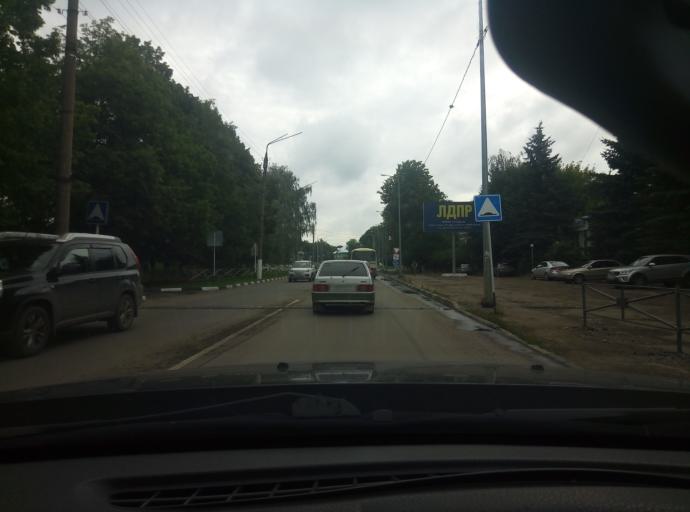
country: RU
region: Tula
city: Donskoy
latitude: 53.9682
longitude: 38.3296
